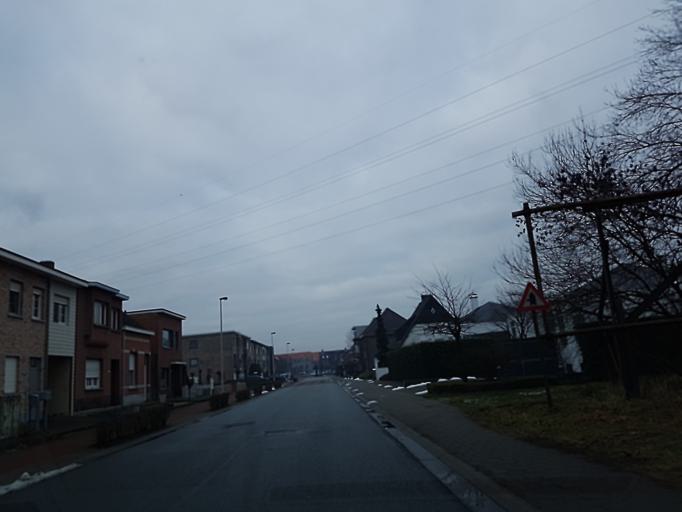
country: BE
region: Flanders
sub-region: Provincie Antwerpen
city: Berlaar
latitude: 51.1474
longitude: 4.6228
